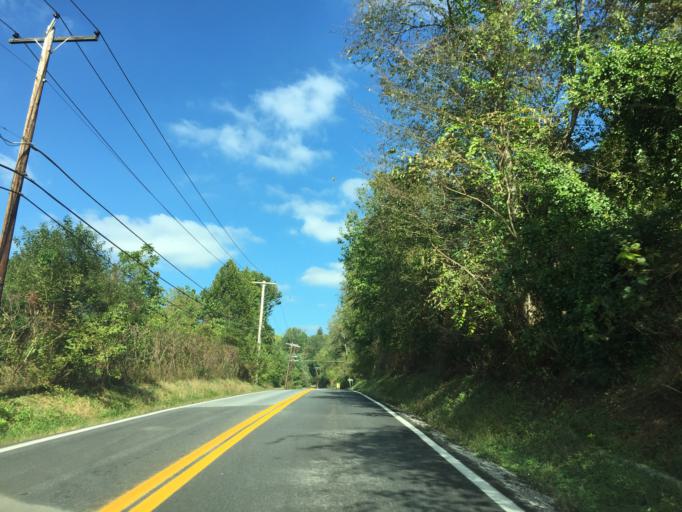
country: US
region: Maryland
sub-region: Baltimore County
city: Perry Hall
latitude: 39.4540
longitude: -76.4668
